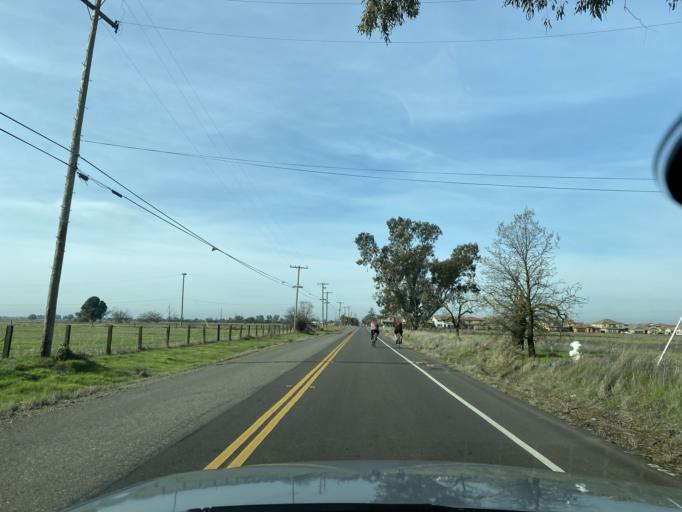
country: US
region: California
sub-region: Sacramento County
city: Elk Grove
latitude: 38.3909
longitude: -121.3888
